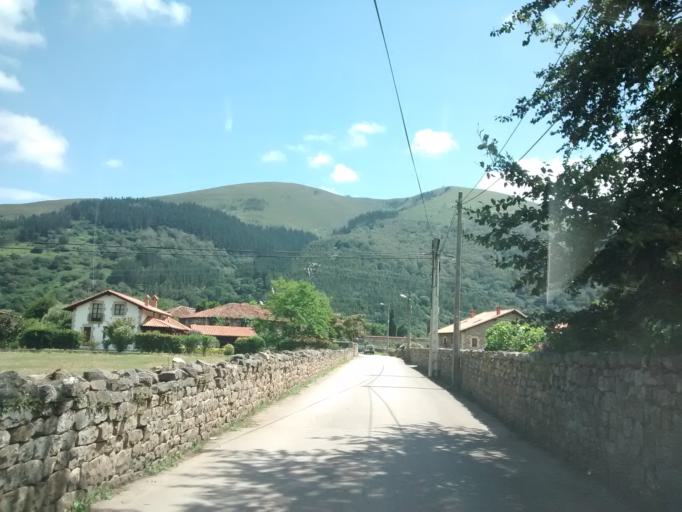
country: ES
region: Cantabria
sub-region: Provincia de Cantabria
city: Ruente
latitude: 43.2197
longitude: -4.3005
